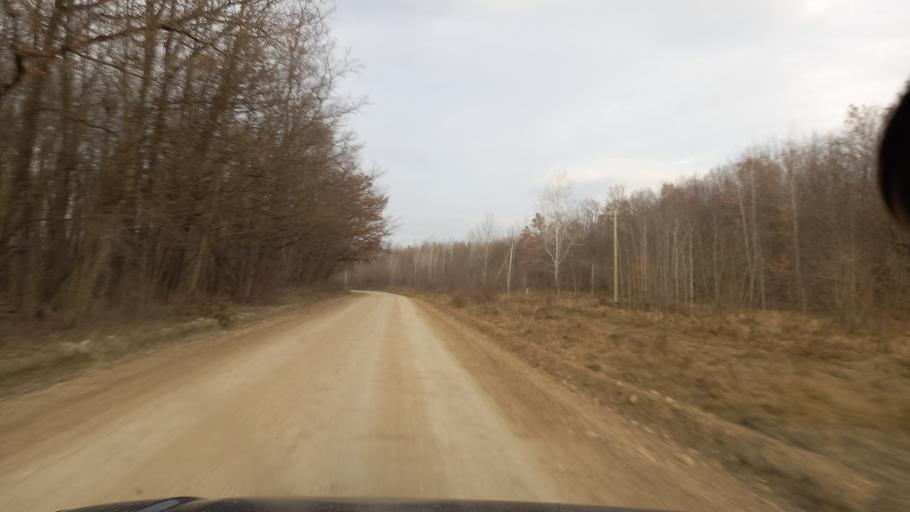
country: RU
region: Adygeya
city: Kamennomostskiy
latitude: 44.1782
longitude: 40.2568
